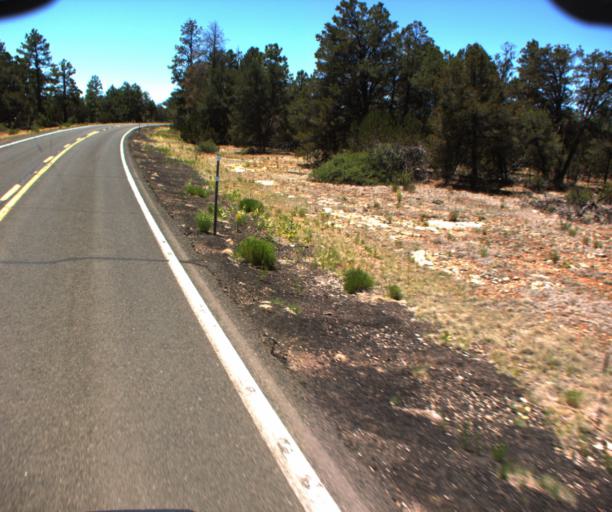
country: US
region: Arizona
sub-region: Gila County
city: Star Valley
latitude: 34.6957
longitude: -111.1071
